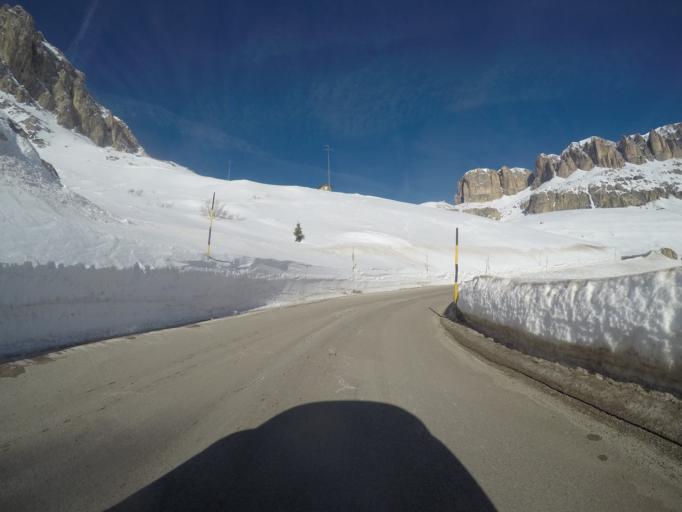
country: IT
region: Trentino-Alto Adige
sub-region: Provincia di Trento
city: Canazei
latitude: 46.4851
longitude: 11.8164
